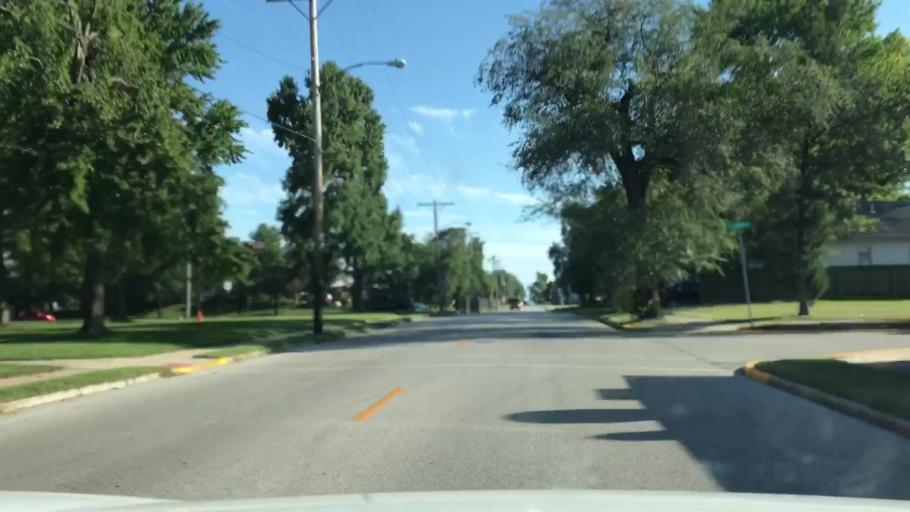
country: US
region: Illinois
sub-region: Madison County
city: Wood River
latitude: 38.8713
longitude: -90.0988
